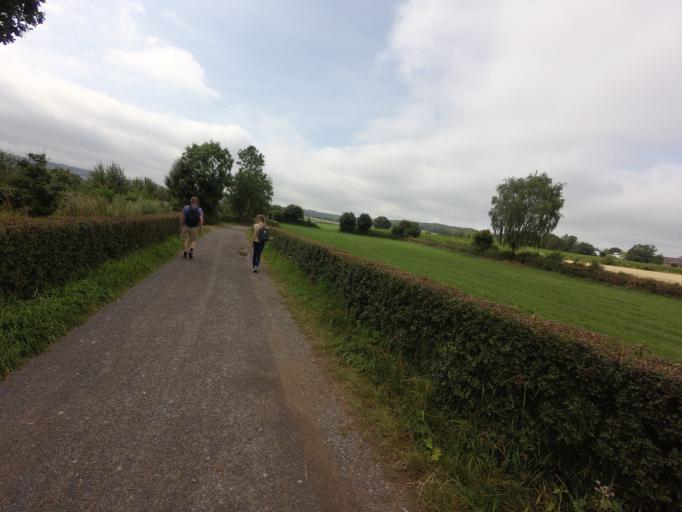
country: NL
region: Limburg
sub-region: Gemeente Vaals
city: Vaals
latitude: 50.7762
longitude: 5.9932
